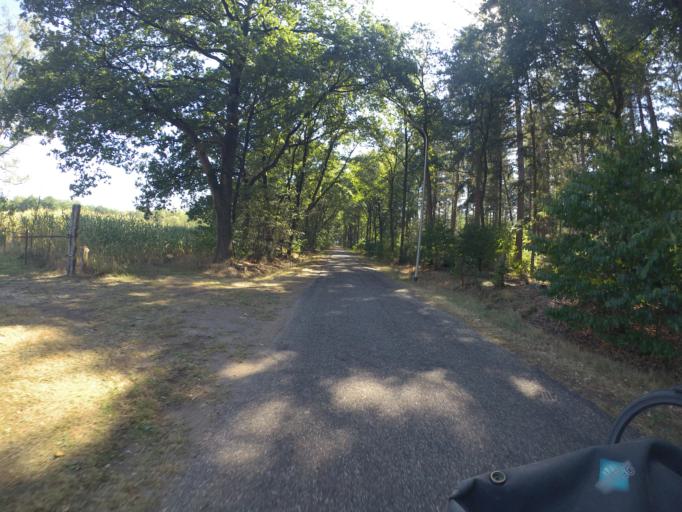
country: NL
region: Overijssel
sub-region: Gemeente Twenterand
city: Den Ham
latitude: 52.4046
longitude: 6.4296
